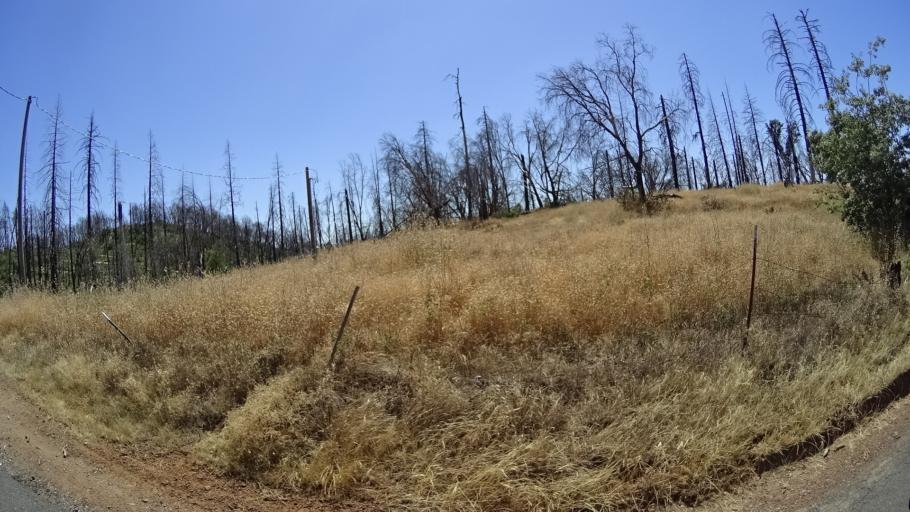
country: US
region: California
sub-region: Calaveras County
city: Mountain Ranch
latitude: 38.2867
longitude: -120.5726
